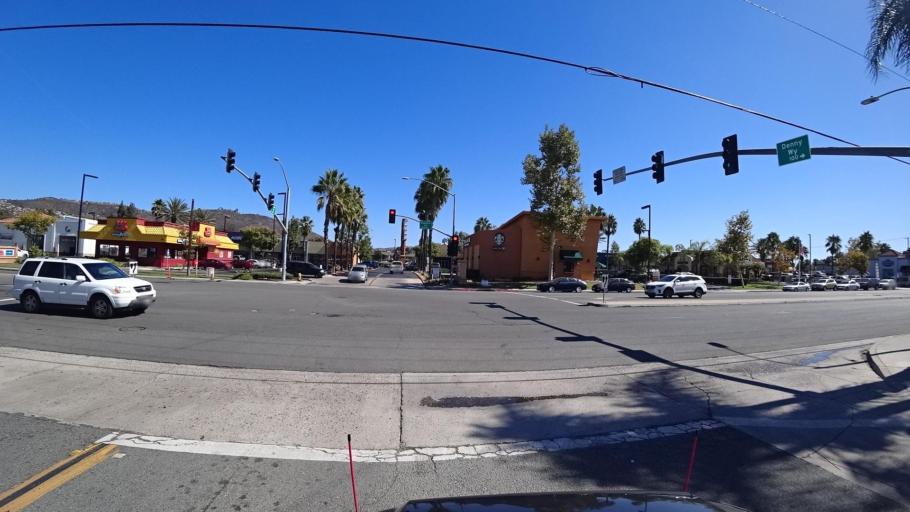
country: US
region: California
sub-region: San Diego County
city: Santee
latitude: 32.8205
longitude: -116.9625
